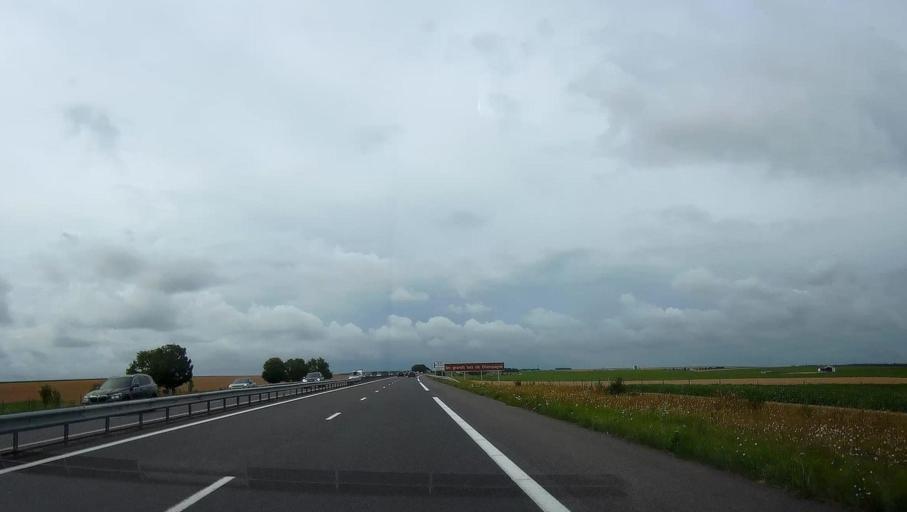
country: FR
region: Champagne-Ardenne
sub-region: Departement de l'Aube
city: Mailly-le-Camp
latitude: 48.7794
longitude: 4.2605
